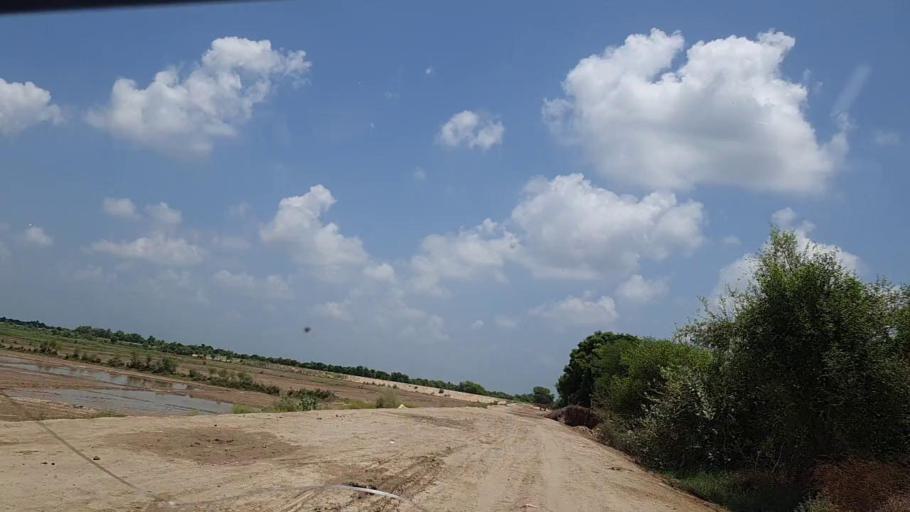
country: PK
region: Sindh
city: Tharu Shah
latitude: 26.9377
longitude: 68.0071
